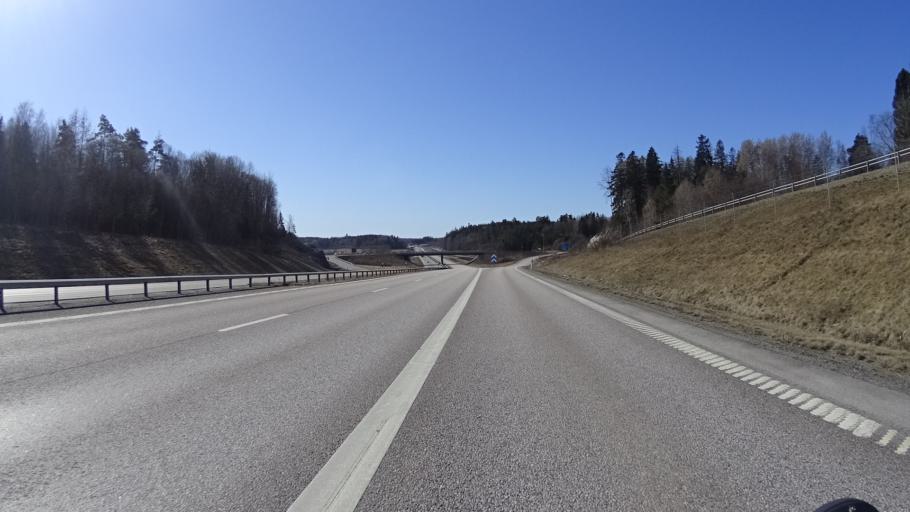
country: SE
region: Stockholm
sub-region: Nynashamns Kommun
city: Osmo
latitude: 58.9805
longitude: 17.9153
